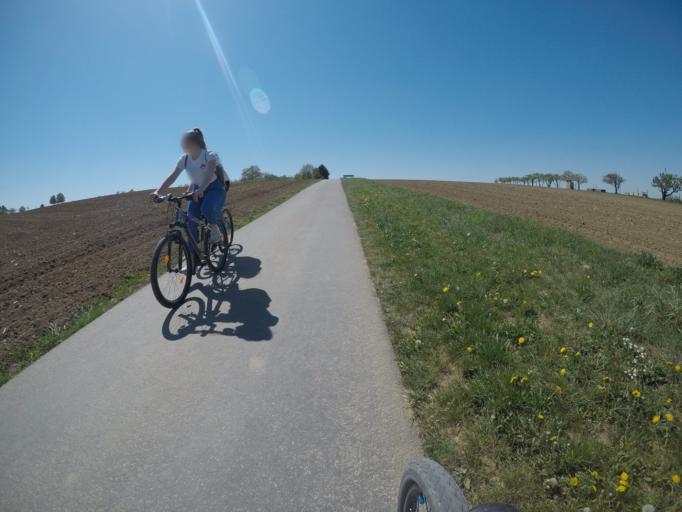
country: DE
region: Baden-Wuerttemberg
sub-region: Regierungsbezirk Stuttgart
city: Fellbach
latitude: 48.8432
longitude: 9.2822
